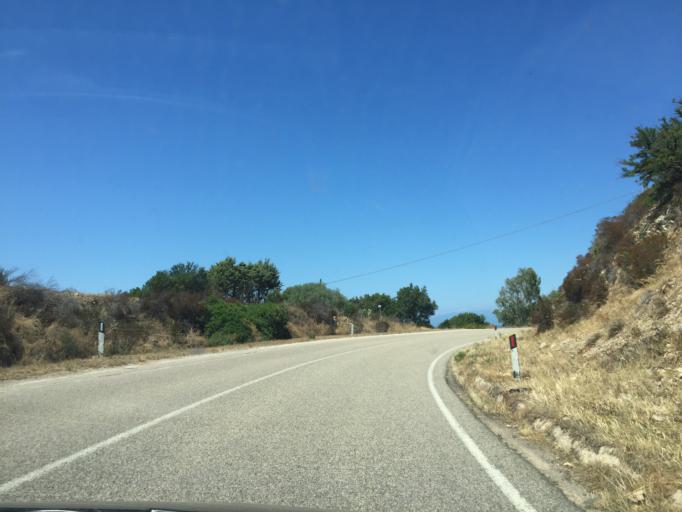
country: IT
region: Sardinia
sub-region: Provincia di Olbia-Tempio
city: Aglientu
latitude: 41.0999
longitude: 9.0830
